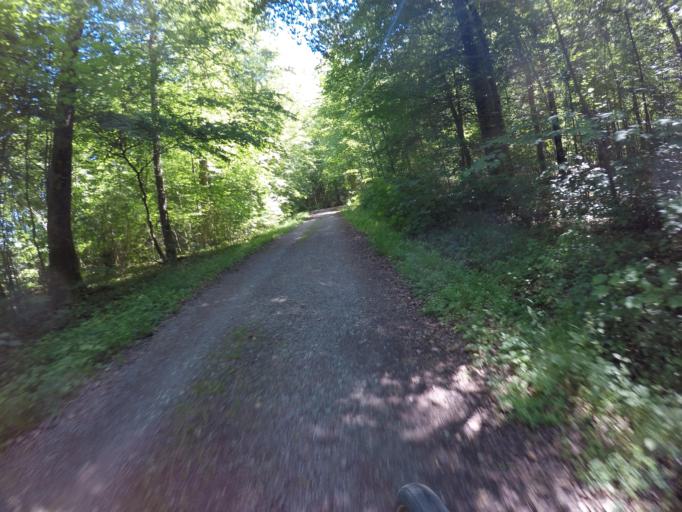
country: DE
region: Baden-Wuerttemberg
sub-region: Regierungsbezirk Stuttgart
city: Gerlingen
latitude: 48.7428
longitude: 9.0839
